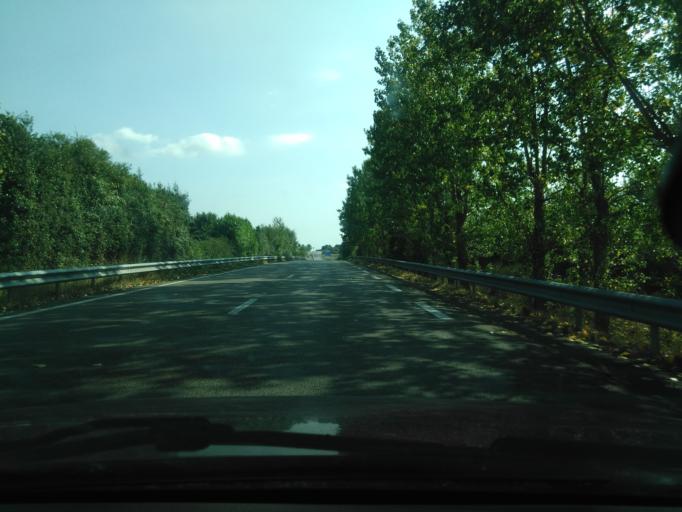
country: FR
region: Pays de la Loire
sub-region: Departement de la Vendee
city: La Roche-sur-Yon
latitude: 46.6320
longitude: -1.4400
